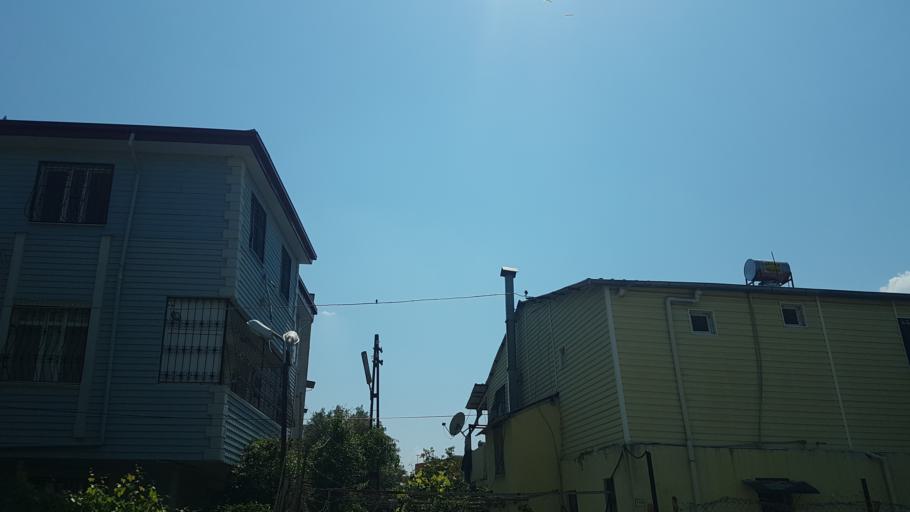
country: TR
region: Adana
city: Adana
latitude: 37.0232
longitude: 35.3694
